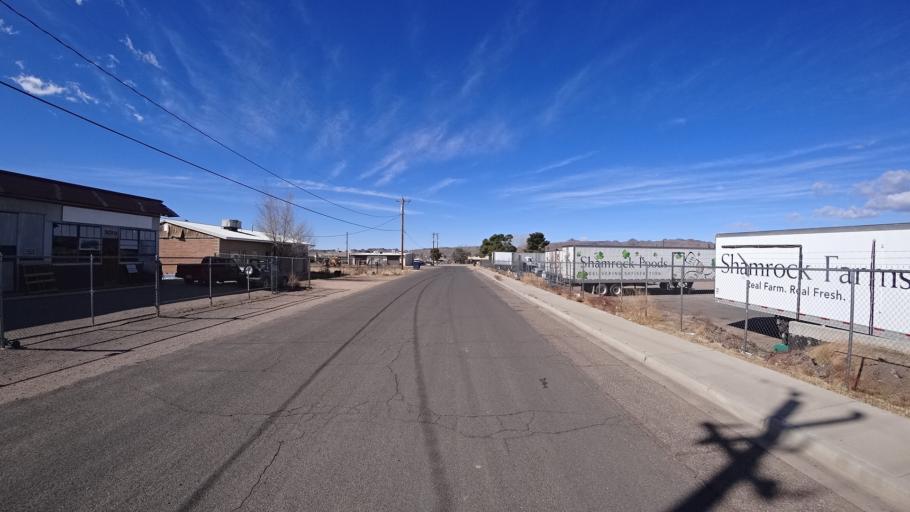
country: US
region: Arizona
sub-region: Mohave County
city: New Kingman-Butler
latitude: 35.2222
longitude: -114.0099
